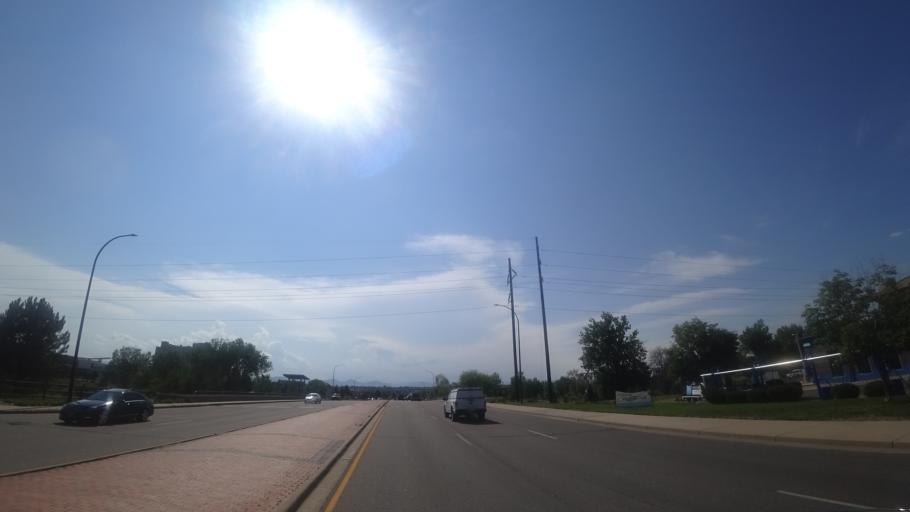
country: US
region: Colorado
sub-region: Arapahoe County
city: Littleton
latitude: 39.6242
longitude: -105.0172
